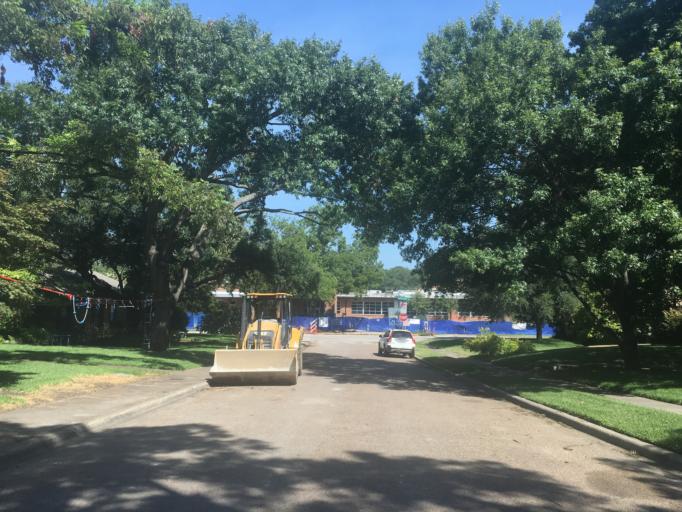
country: US
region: Texas
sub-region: Dallas County
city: Richardson
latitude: 32.8725
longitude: -96.7224
